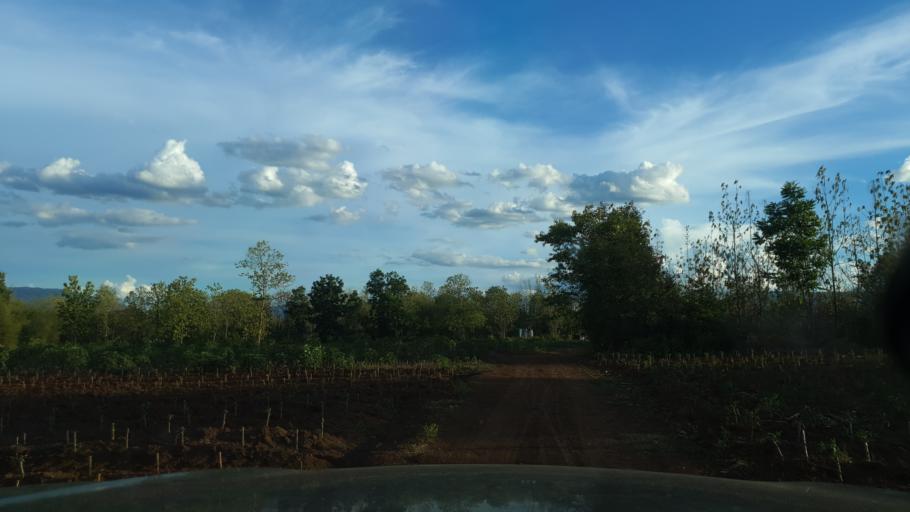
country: TH
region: Lampang
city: Sop Prap
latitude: 17.9610
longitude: 99.3520
